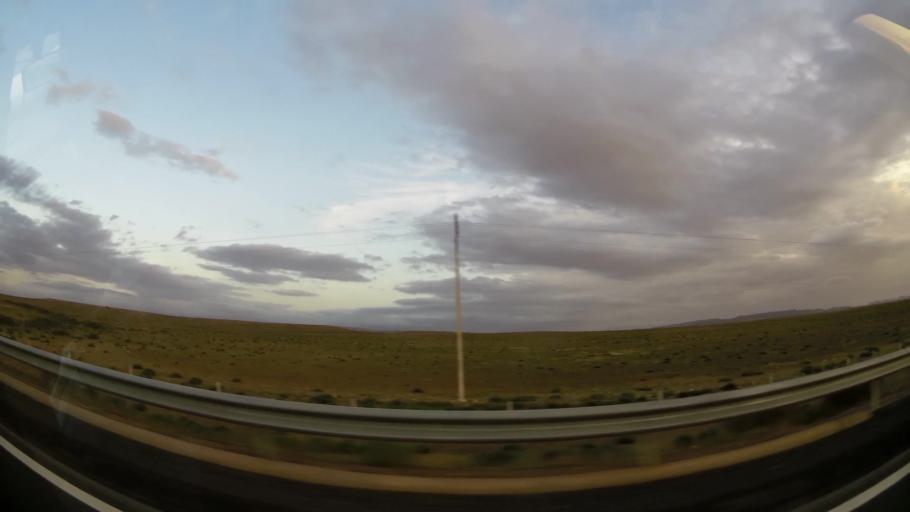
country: MA
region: Oriental
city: Taourirt
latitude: 34.5489
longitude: -2.8843
